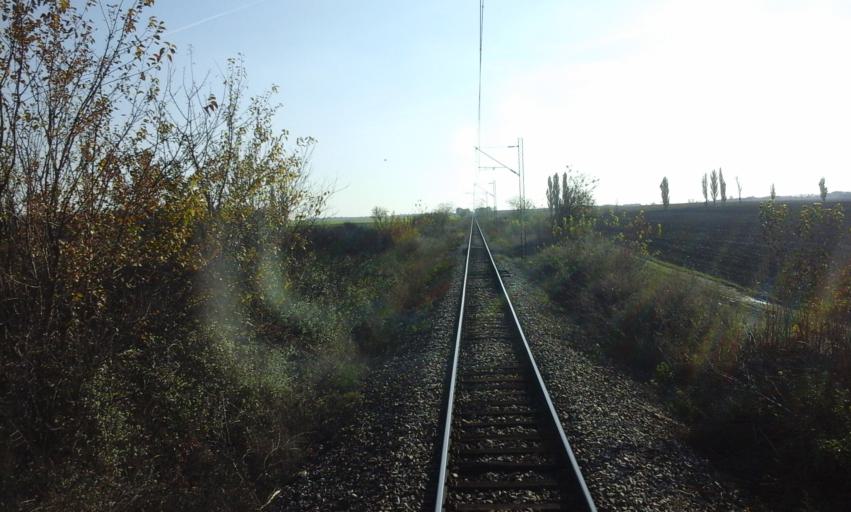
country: RS
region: Autonomna Pokrajina Vojvodina
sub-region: Severnobacki Okrug
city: Backa Topola
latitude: 45.7795
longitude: 19.6478
